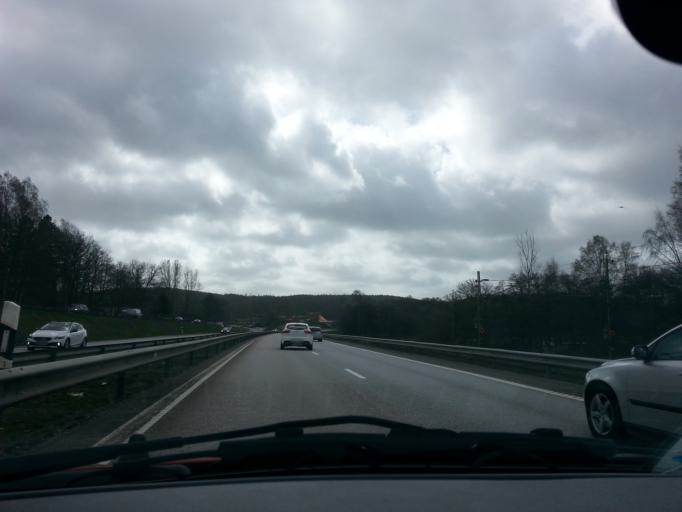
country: SE
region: Vaestra Goetaland
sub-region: Lerums Kommun
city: Lerum
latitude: 57.7570
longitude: 12.2528
